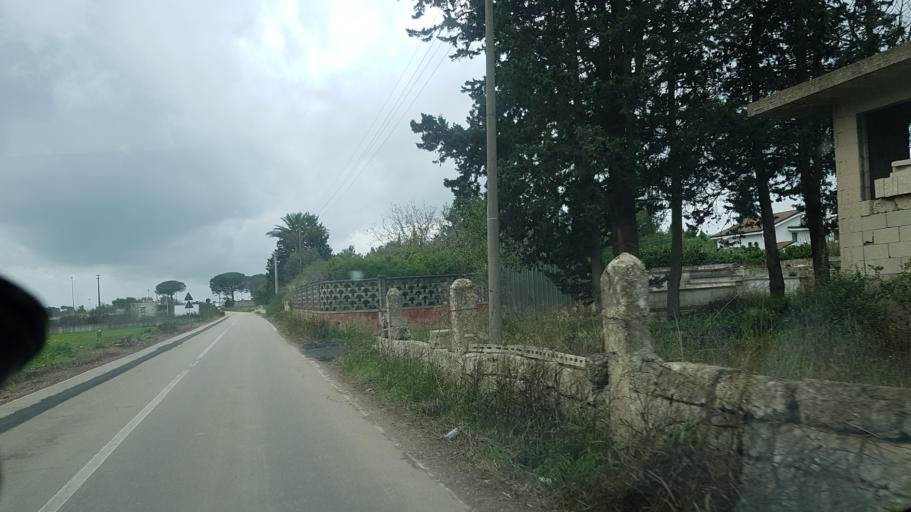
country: IT
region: Apulia
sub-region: Provincia di Lecce
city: Novoli
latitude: 40.3708
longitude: 18.0462
